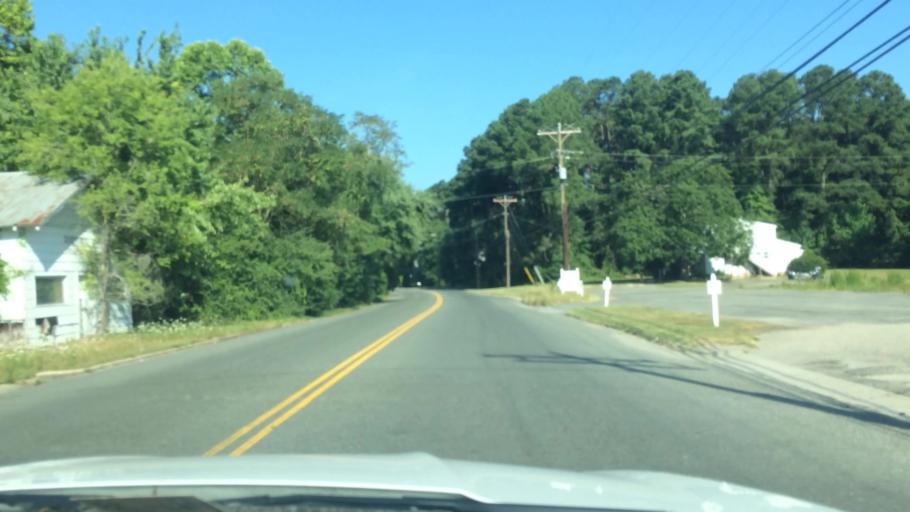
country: US
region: Virginia
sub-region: Lancaster County
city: Lancaster
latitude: 37.7690
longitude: -76.4602
